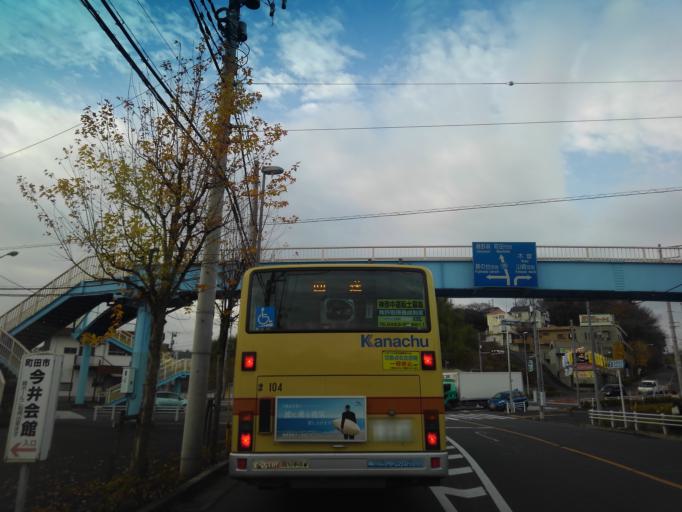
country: JP
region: Tokyo
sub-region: Machida-shi
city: Machida
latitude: 35.5727
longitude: 139.4435
